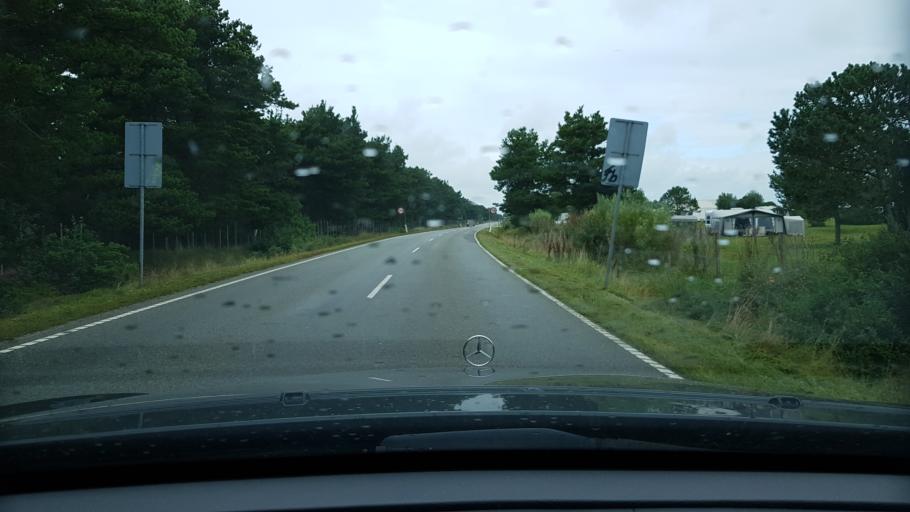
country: DK
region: North Denmark
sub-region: Alborg Kommune
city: Hals
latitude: 56.8221
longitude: 10.2693
